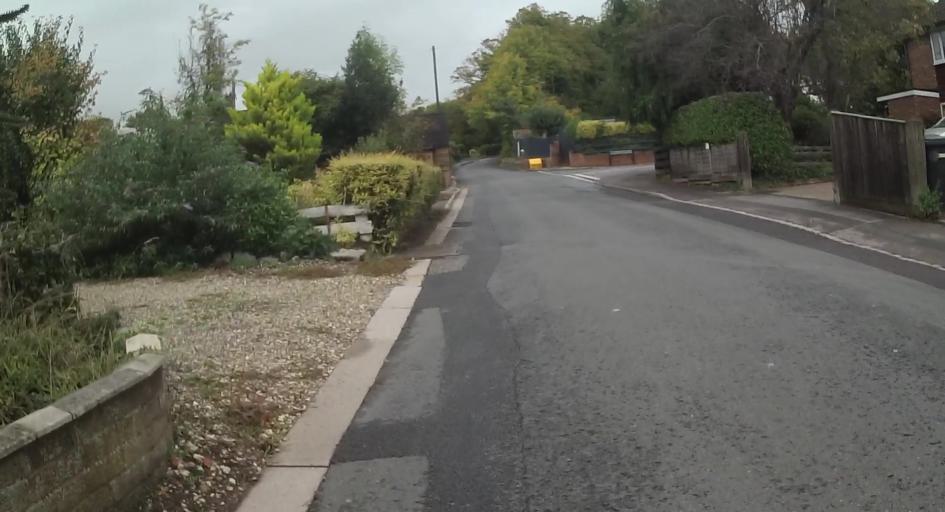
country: GB
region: England
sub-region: Hampshire
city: Tadley
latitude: 51.3980
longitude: -1.1783
